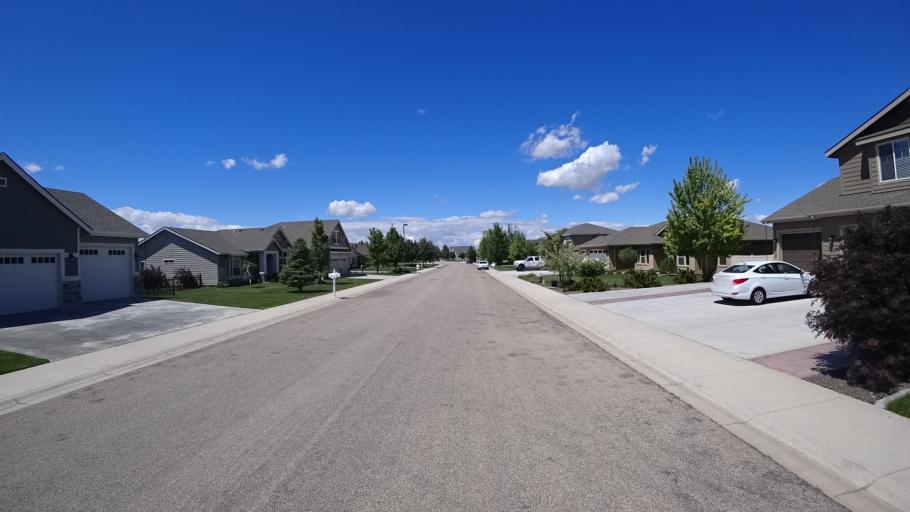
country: US
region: Idaho
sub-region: Ada County
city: Kuna
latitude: 43.5132
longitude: -116.4303
